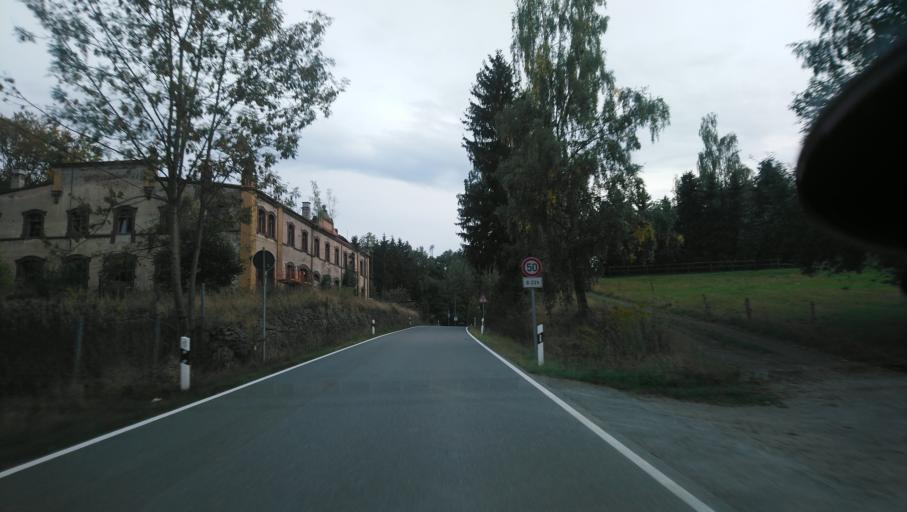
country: DE
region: Saxony
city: Wiesa
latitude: 50.6001
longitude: 12.9955
